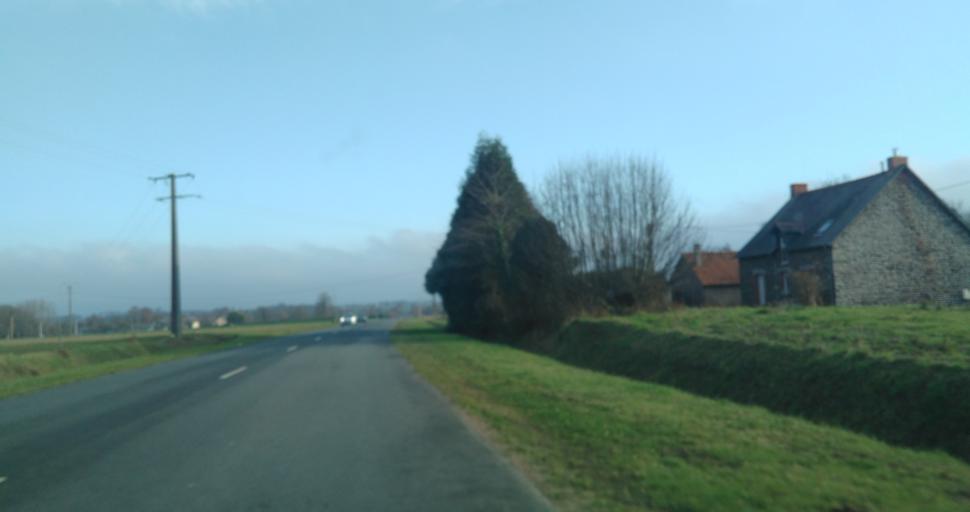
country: FR
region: Brittany
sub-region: Departement d'Ille-et-Vilaine
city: Saint-Meen-le-Grand
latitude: 48.1772
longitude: -2.1405
